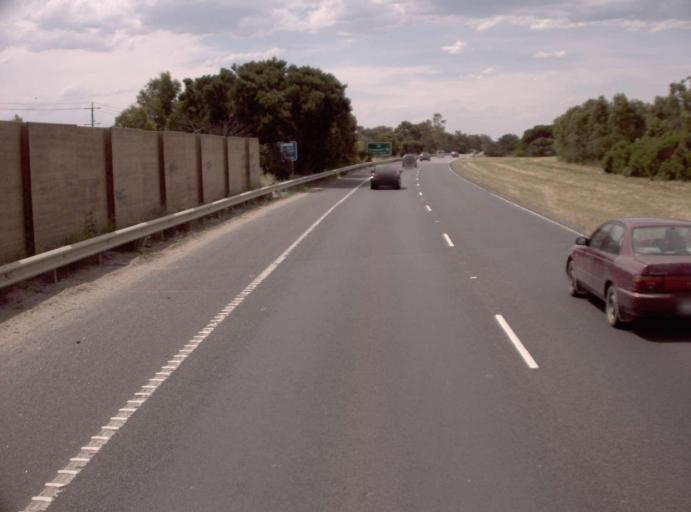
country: AU
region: Victoria
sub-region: Kingston
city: Patterson Lakes
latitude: -38.0829
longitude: 145.1485
